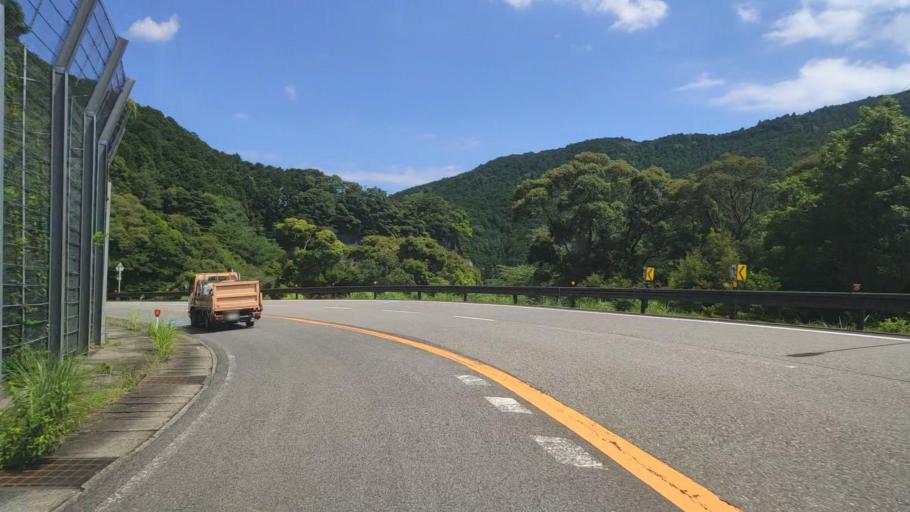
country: JP
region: Mie
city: Owase
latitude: 33.9207
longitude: 136.1014
